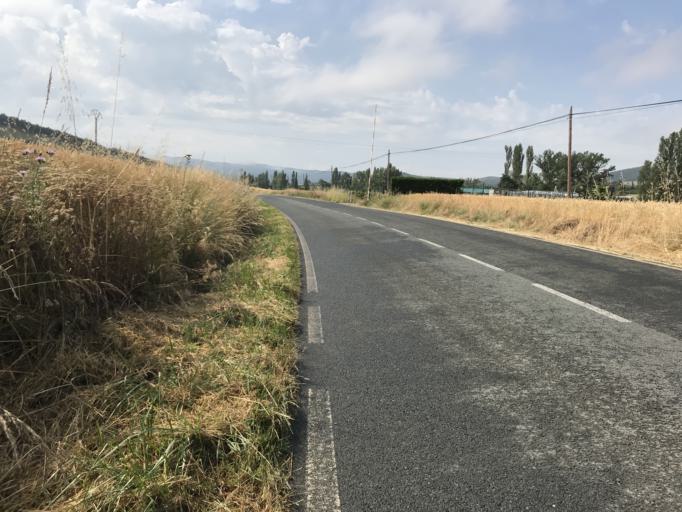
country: ES
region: Basque Country
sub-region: Provincia de Alava
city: Gasteiz / Vitoria
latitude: 42.8255
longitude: -2.6501
